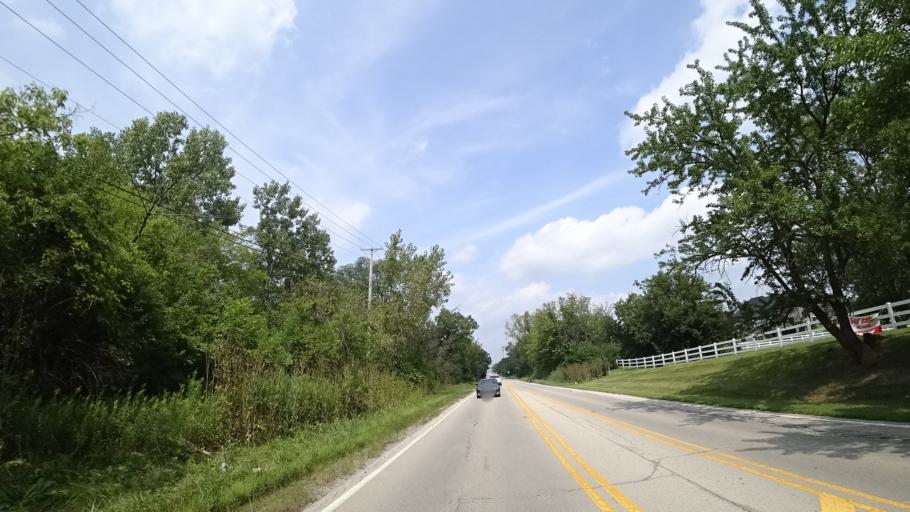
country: US
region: Illinois
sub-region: Cook County
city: Orland Park
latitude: 41.6257
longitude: -87.8923
